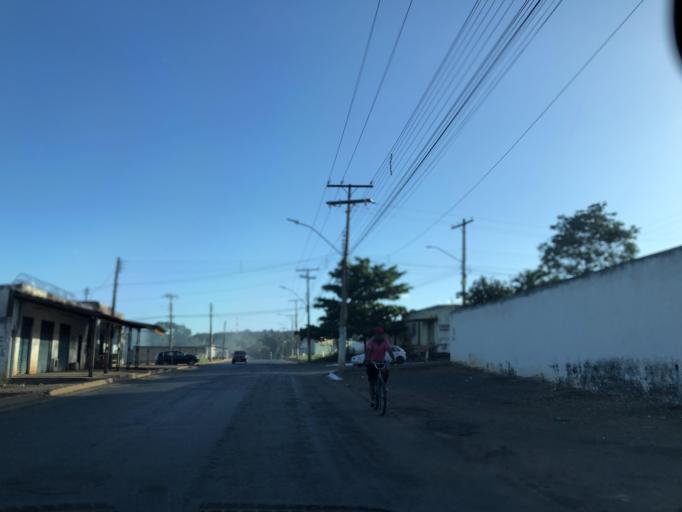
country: BR
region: Goias
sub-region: Luziania
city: Luziania
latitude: -16.2593
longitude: -47.9520
